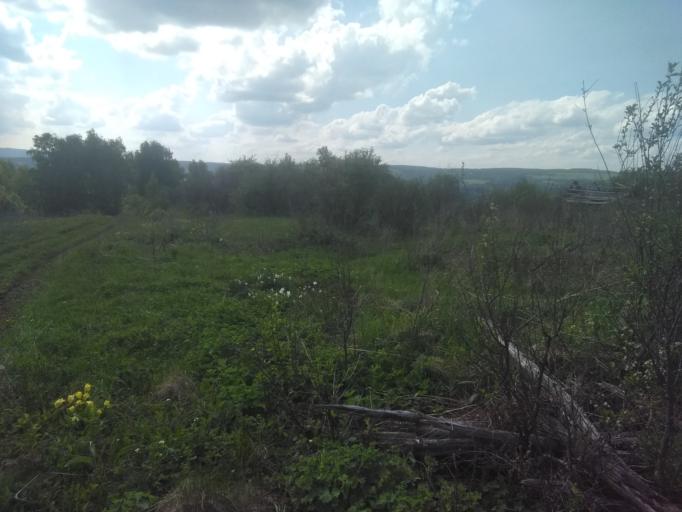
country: RU
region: Chelyabinsk
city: Sim
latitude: 55.0019
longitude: 57.7241
